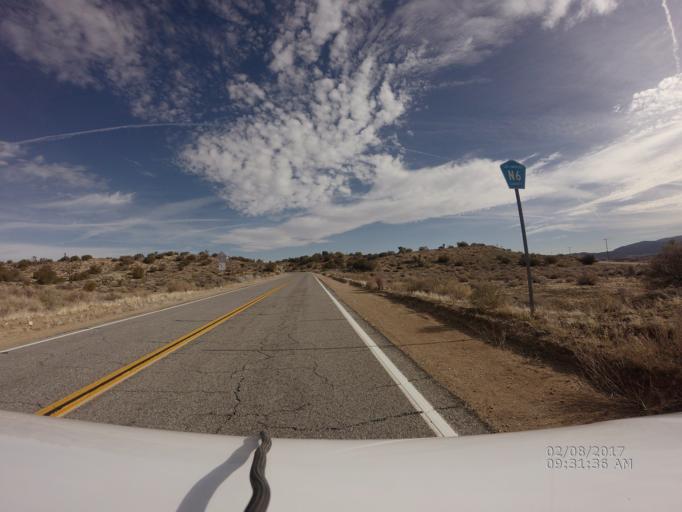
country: US
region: California
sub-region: Los Angeles County
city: Littlerock
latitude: 34.4577
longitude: -117.9013
